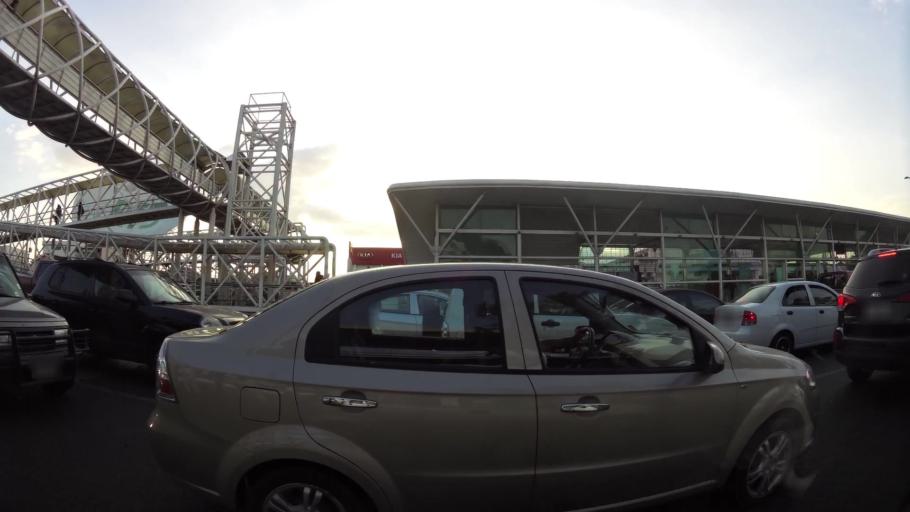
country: EC
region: Guayas
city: Eloy Alfaro
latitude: -2.1469
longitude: -79.8857
